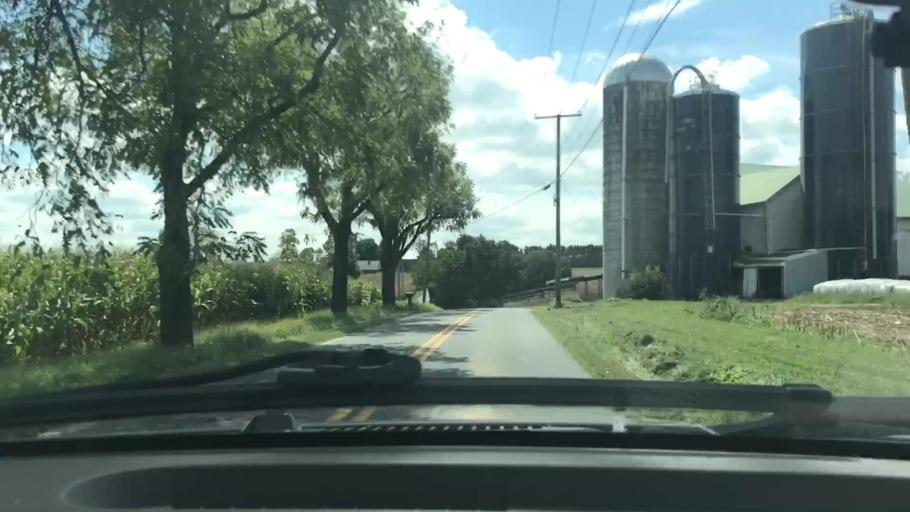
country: US
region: Pennsylvania
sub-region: Lancaster County
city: Landisville
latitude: 40.1086
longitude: -76.3864
